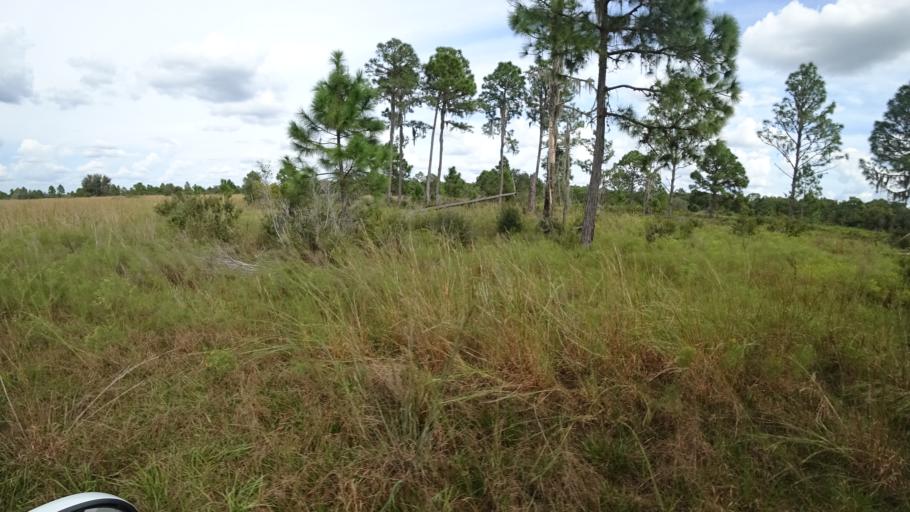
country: US
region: Florida
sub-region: Hillsborough County
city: Wimauma
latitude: 27.5492
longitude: -82.1354
